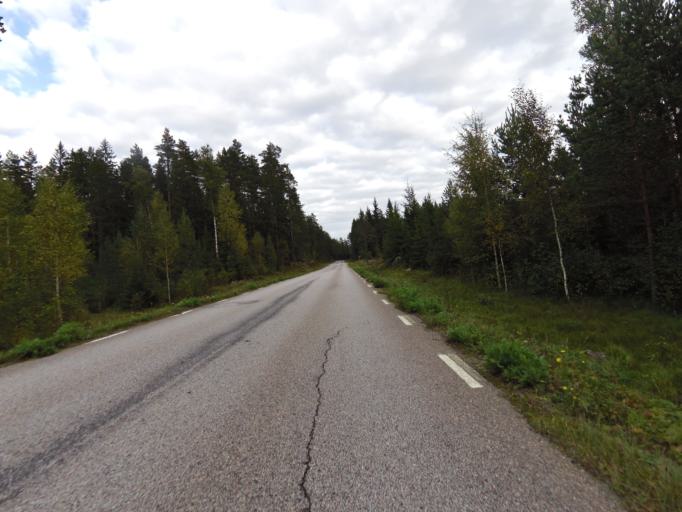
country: SE
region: Gaevleborg
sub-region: Gavle Kommun
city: Valbo
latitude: 60.6702
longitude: 16.9055
